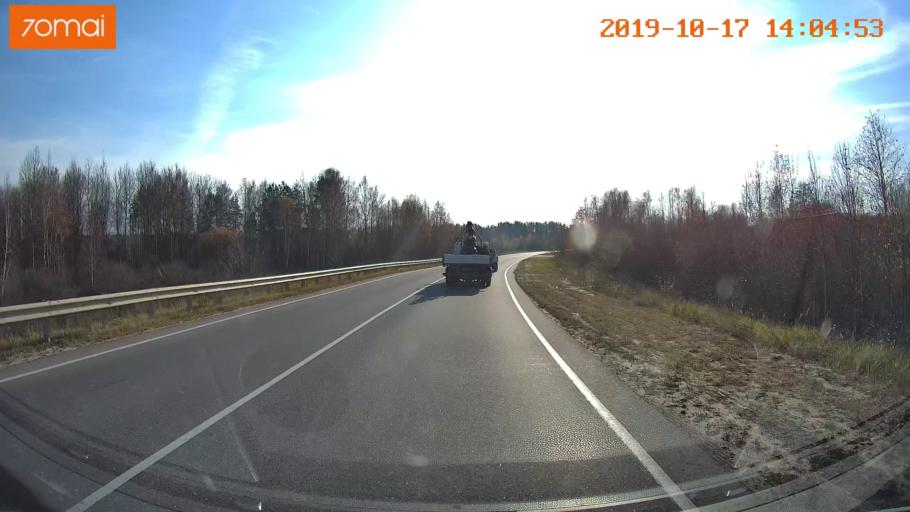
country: RU
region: Rjazan
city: Spas-Klepiki
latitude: 55.1212
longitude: 40.1330
